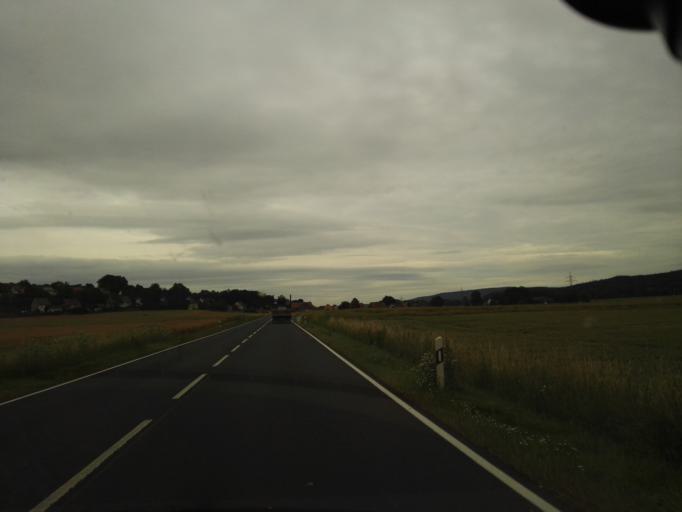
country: DE
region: Bavaria
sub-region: Upper Franconia
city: Redwitz an der Rodach
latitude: 50.1554
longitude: 11.2067
